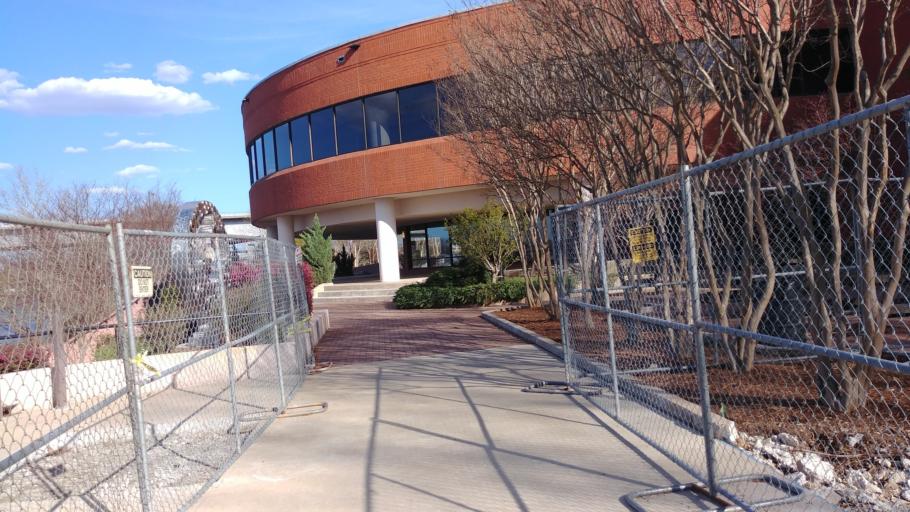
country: US
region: Arkansas
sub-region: Pulaski County
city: Little Rock
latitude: 34.7497
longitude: -92.2714
